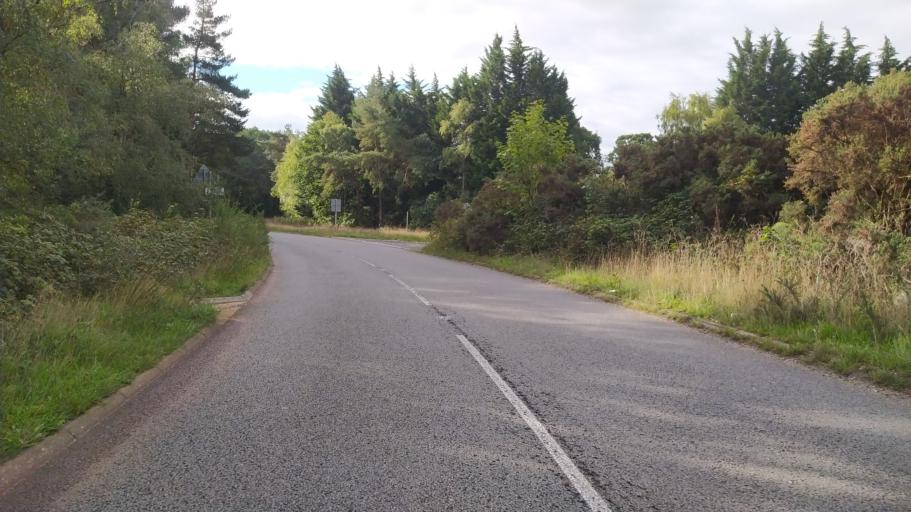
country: GB
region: England
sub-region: Dorset
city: Christchurch
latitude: 50.7647
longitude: -1.8097
